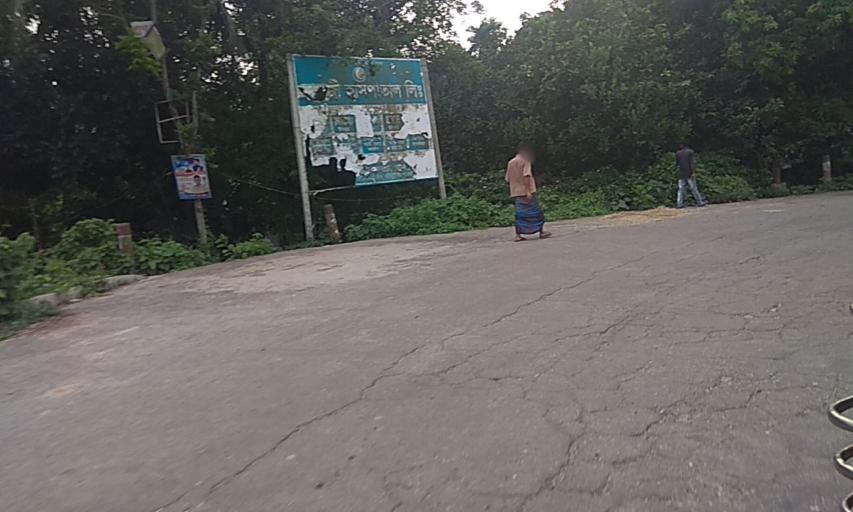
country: BD
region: Dhaka
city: Dohar
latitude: 23.4548
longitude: 90.0064
